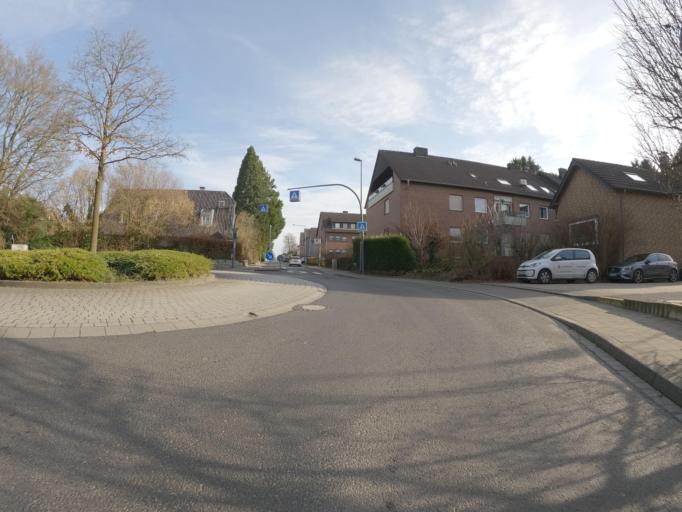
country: DE
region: North Rhine-Westphalia
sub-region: Regierungsbezirk Koln
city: Aachen
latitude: 50.7429
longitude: 6.1529
